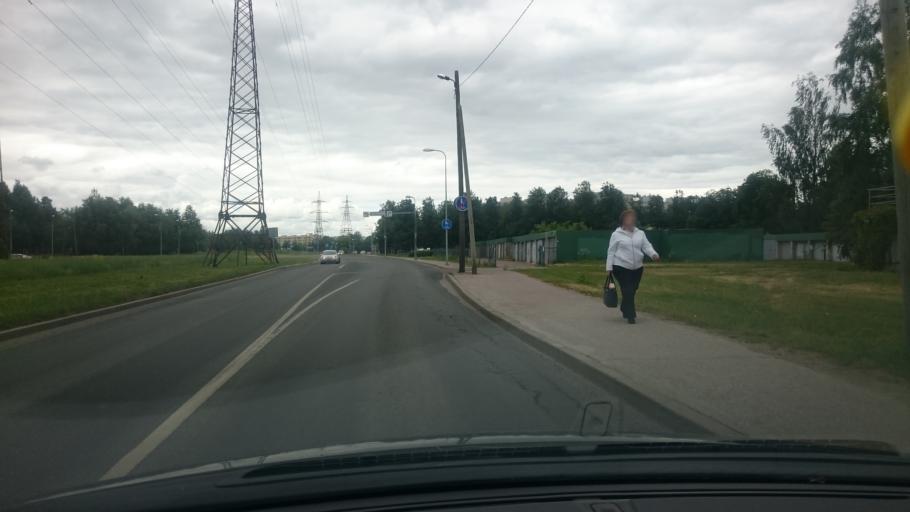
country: EE
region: Harju
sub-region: Saue vald
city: Laagri
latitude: 59.4090
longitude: 24.6498
